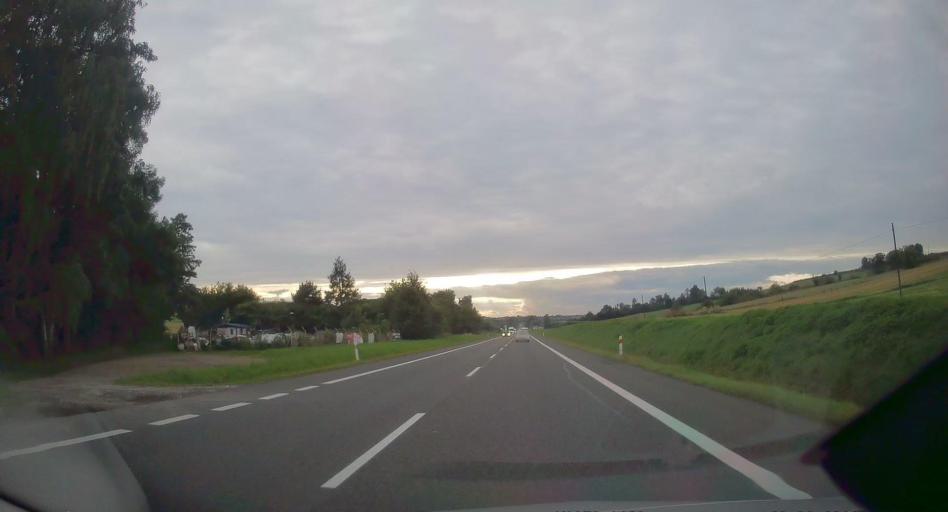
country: PL
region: Lesser Poland Voivodeship
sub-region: Powiat wielicki
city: Szarow
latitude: 49.9829
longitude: 20.2258
